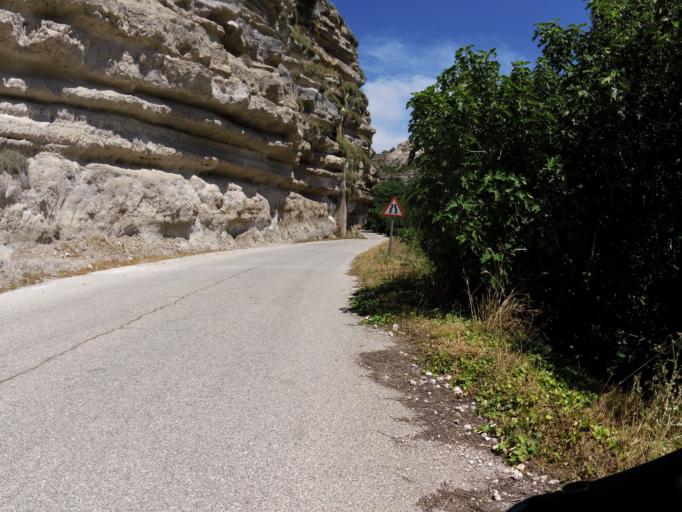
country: ES
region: Castille-La Mancha
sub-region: Provincia de Albacete
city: Jorquera
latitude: 39.1741
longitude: -1.5232
